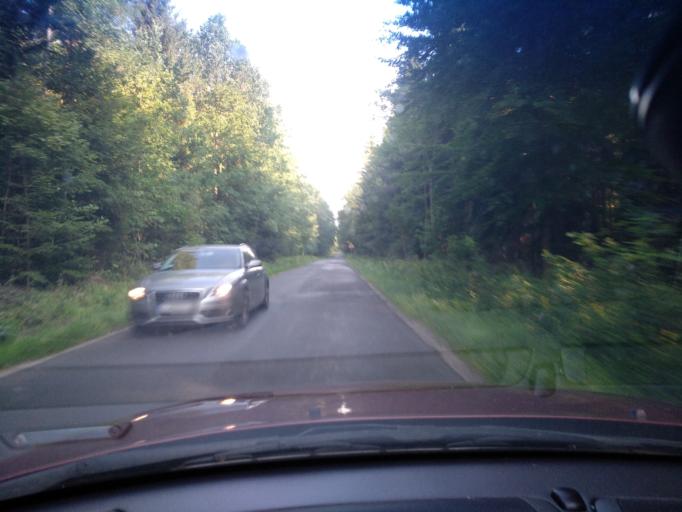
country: PL
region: Lower Silesian Voivodeship
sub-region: Powiat lubanski
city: Swieradow-Zdroj
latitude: 50.9594
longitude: 15.3027
